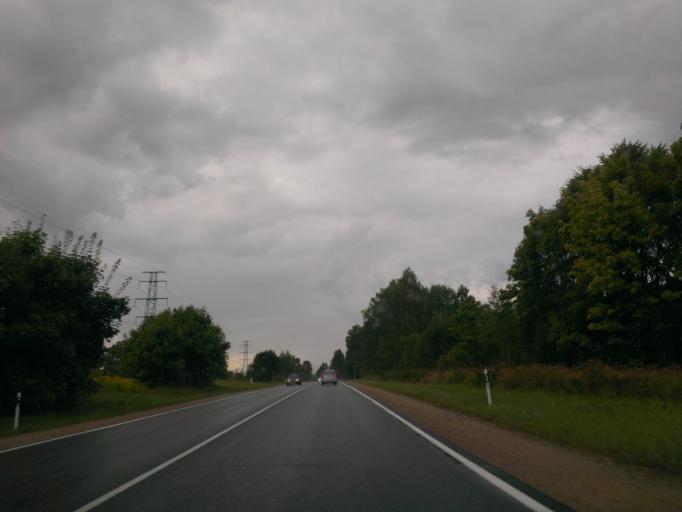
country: LV
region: Kegums
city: Kegums
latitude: 56.7568
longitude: 24.7003
